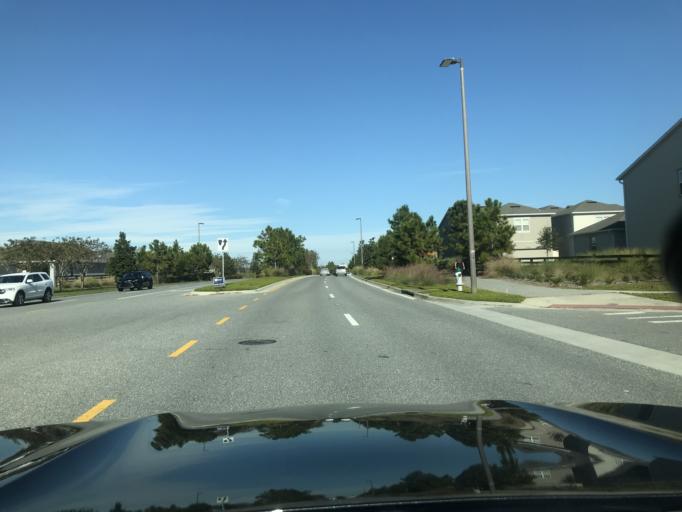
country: US
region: Florida
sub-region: Orange County
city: Oakland
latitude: 28.4637
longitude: -81.6264
